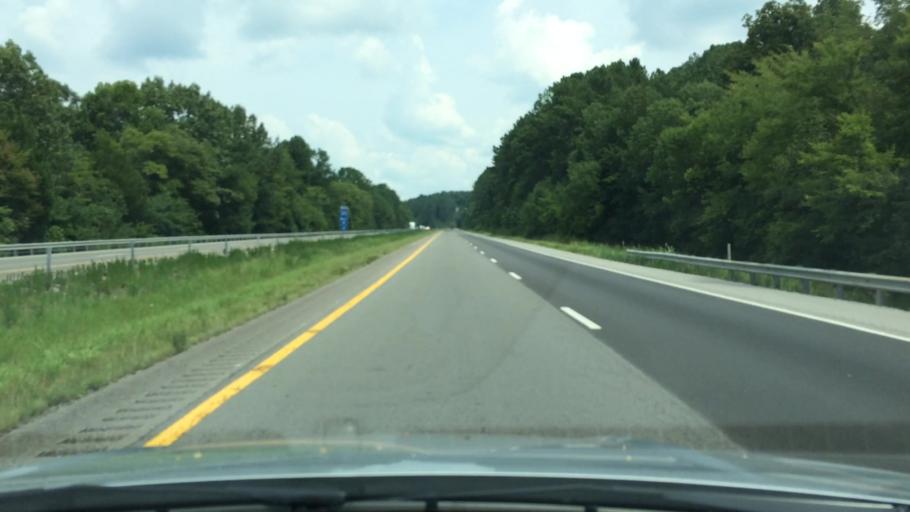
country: US
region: Tennessee
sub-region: Marshall County
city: Cornersville
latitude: 35.2525
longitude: -86.8828
